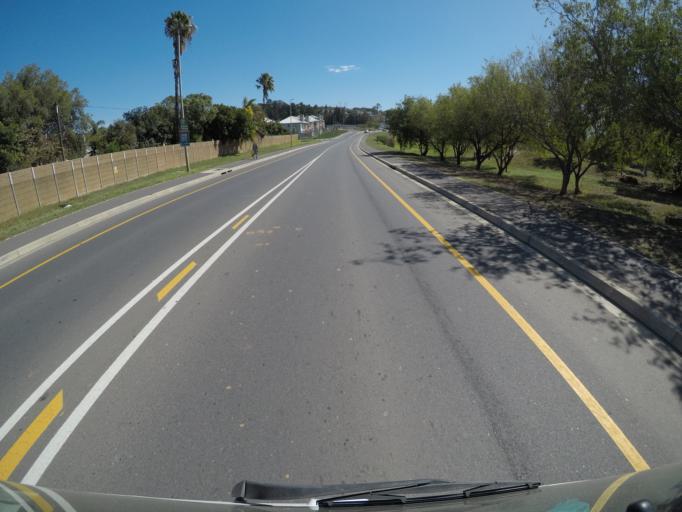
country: ZA
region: Western Cape
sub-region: City of Cape Town
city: Kraaifontein
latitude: -33.8293
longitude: 18.6391
